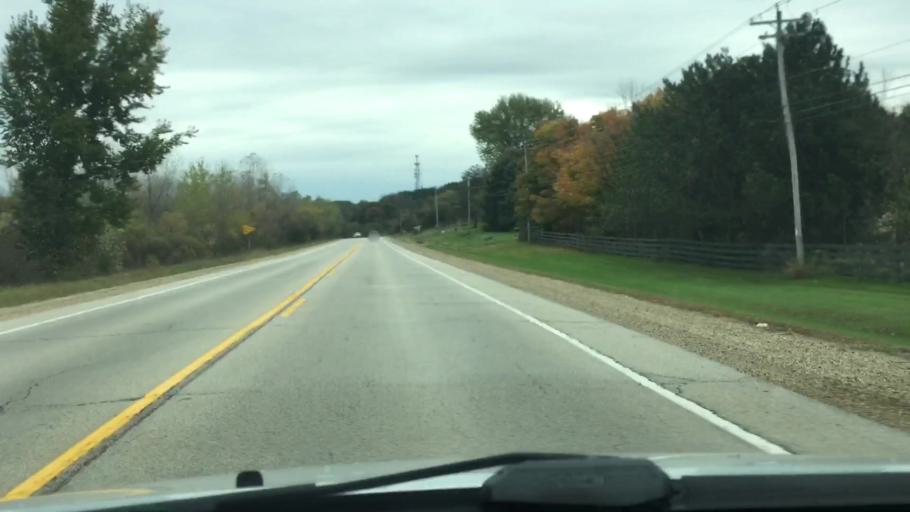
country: US
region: Wisconsin
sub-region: Waukesha County
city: Wales
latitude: 43.0203
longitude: -88.3339
